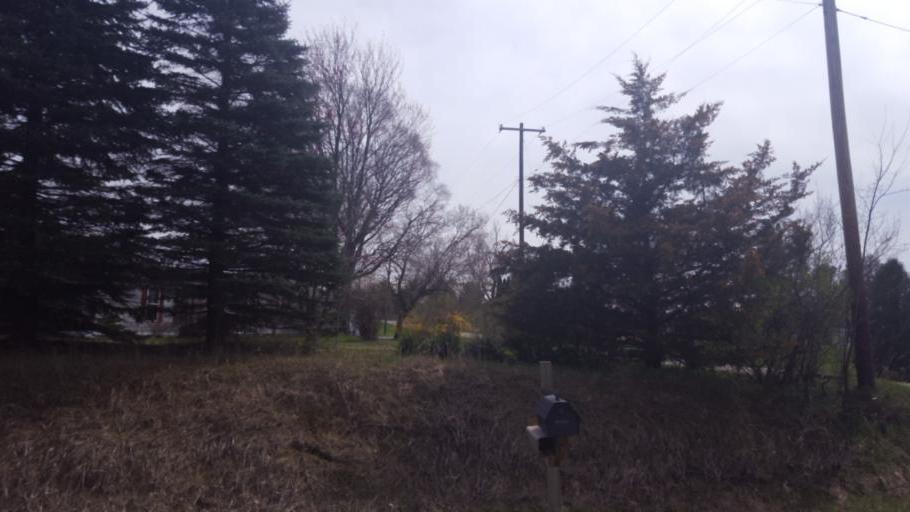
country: US
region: Michigan
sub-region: Gladwin County
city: Gladwin
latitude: 43.9879
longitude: -84.5449
